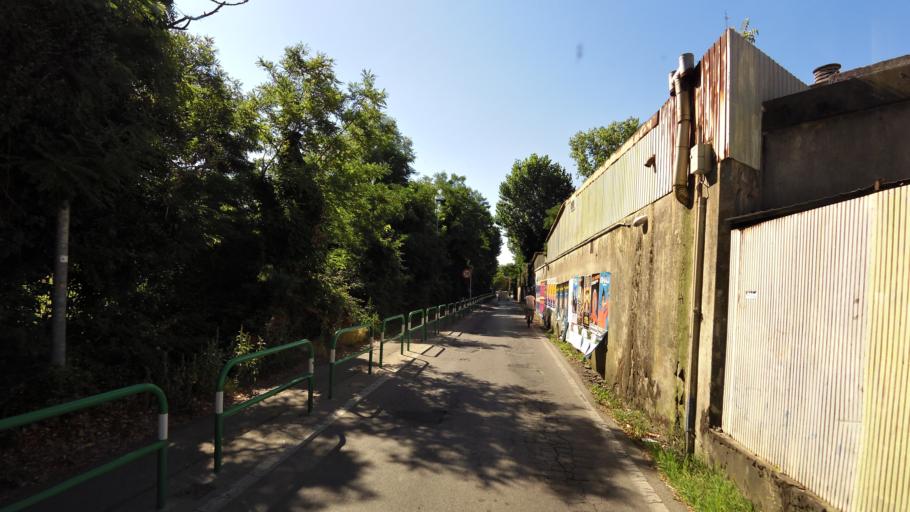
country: IT
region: Veneto
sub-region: Provincia di Venezia
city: Chioggia
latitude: 45.2108
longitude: 12.2910
